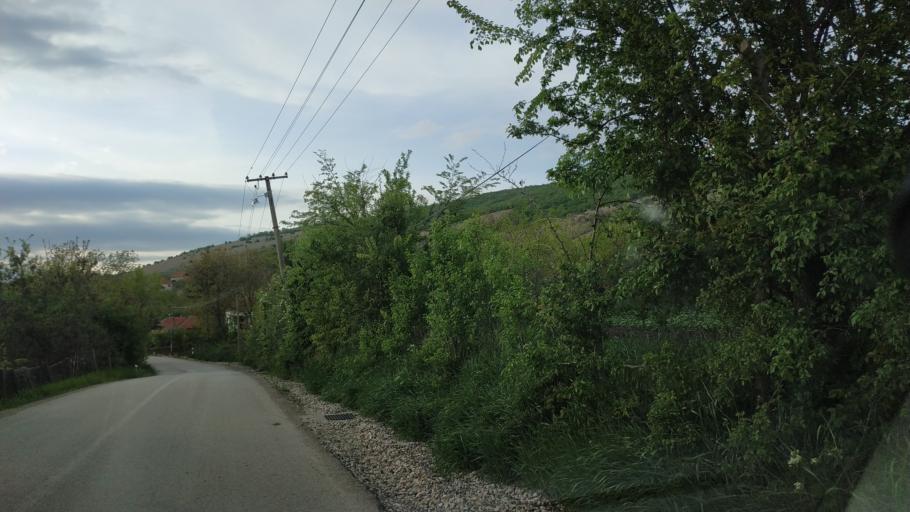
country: RS
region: Central Serbia
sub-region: Zajecarski Okrug
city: Soko Banja
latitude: 43.5264
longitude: 21.8572
